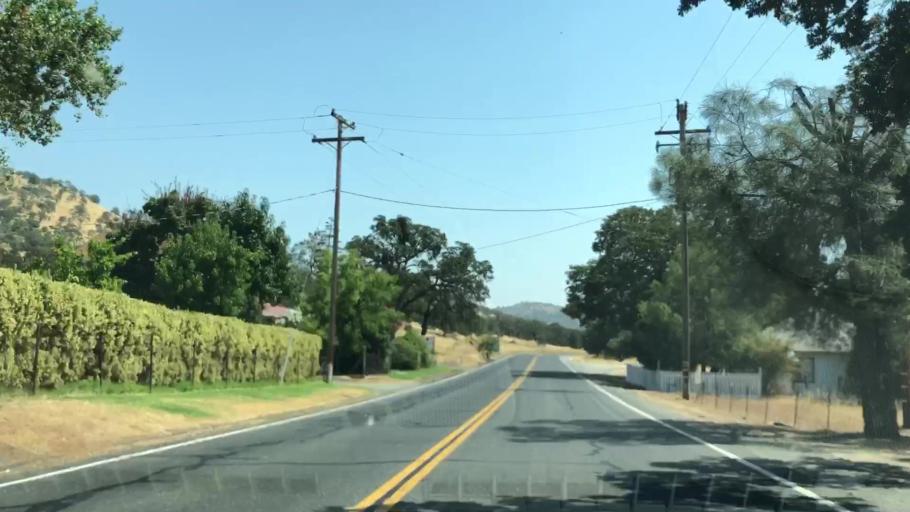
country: US
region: California
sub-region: Calaveras County
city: Copperopolis
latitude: 37.9755
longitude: -120.6350
